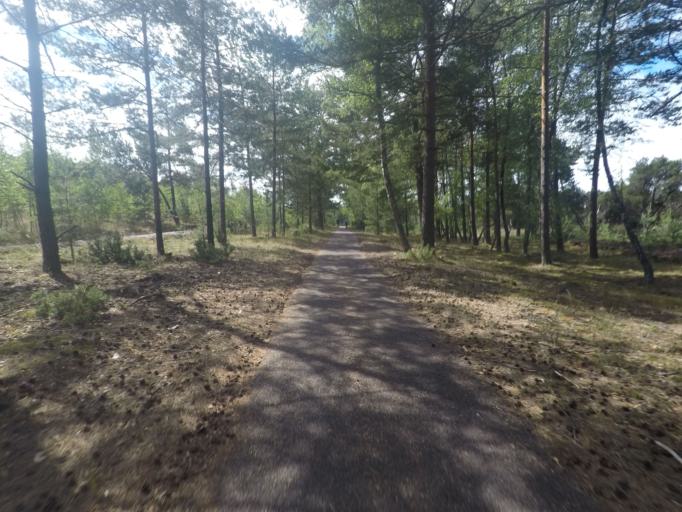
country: LT
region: Klaipedos apskritis
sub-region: Klaipeda
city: Klaipeda
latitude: 55.5696
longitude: 21.1131
